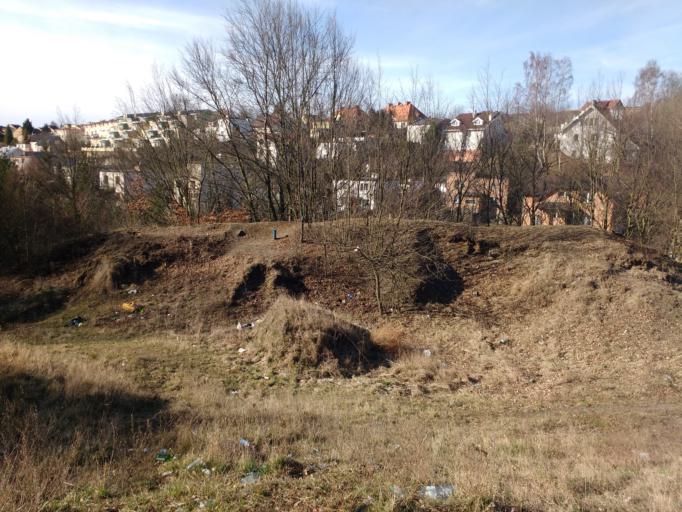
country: PL
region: Pomeranian Voivodeship
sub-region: Gdynia
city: Wielki Kack
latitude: 54.4762
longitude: 18.5124
